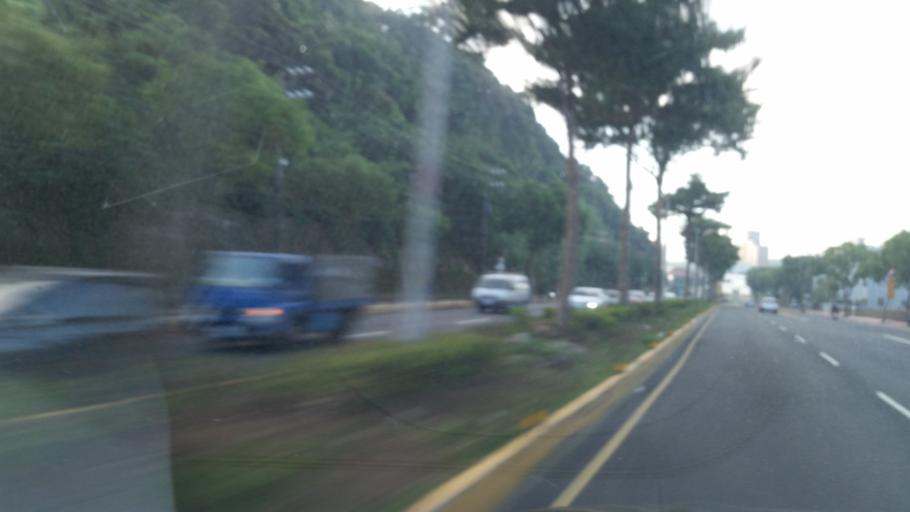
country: TW
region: Taiwan
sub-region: Taoyuan
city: Taoyuan
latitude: 25.0111
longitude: 121.3465
